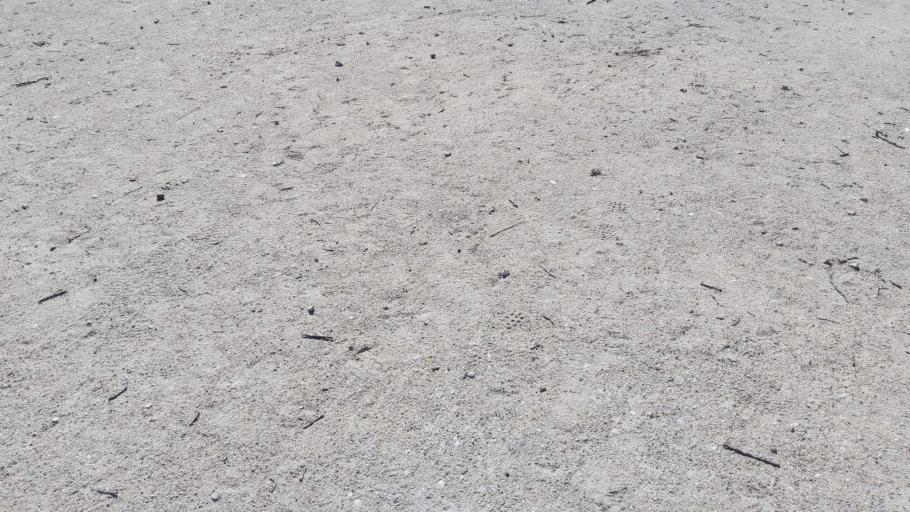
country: FR
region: Rhone-Alpes
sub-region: Departement de l'Ardeche
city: Villevocance
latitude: 45.2289
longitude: 4.5951
